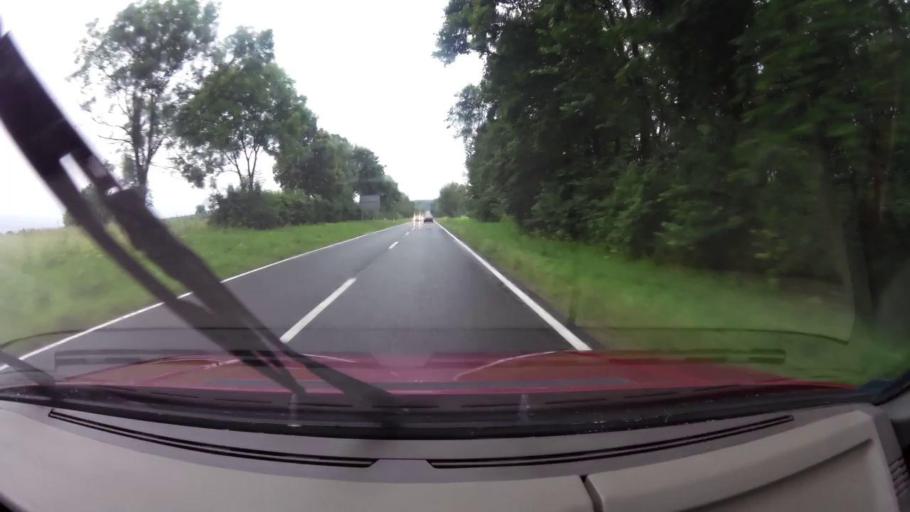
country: PL
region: West Pomeranian Voivodeship
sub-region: Powiat stargardzki
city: Marianowo
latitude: 53.4296
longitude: 15.2908
